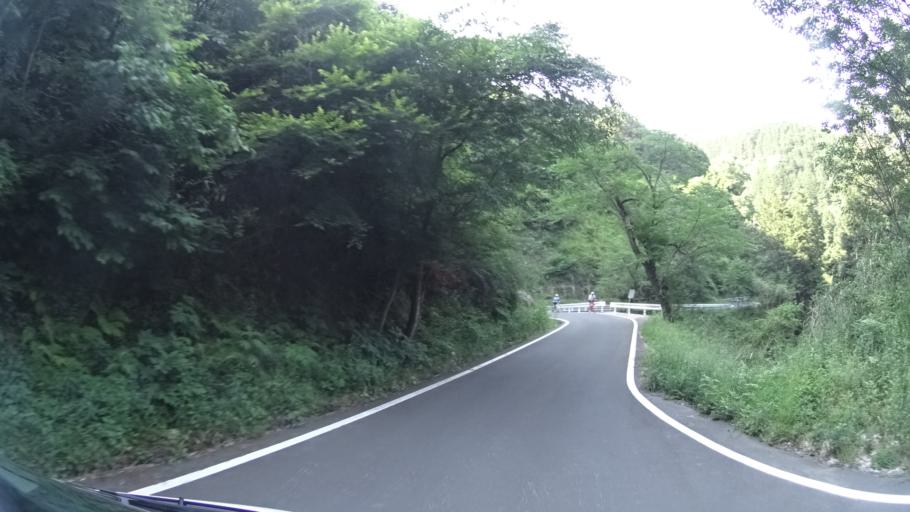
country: JP
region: Kyoto
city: Miyazu
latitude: 35.5670
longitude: 135.1377
